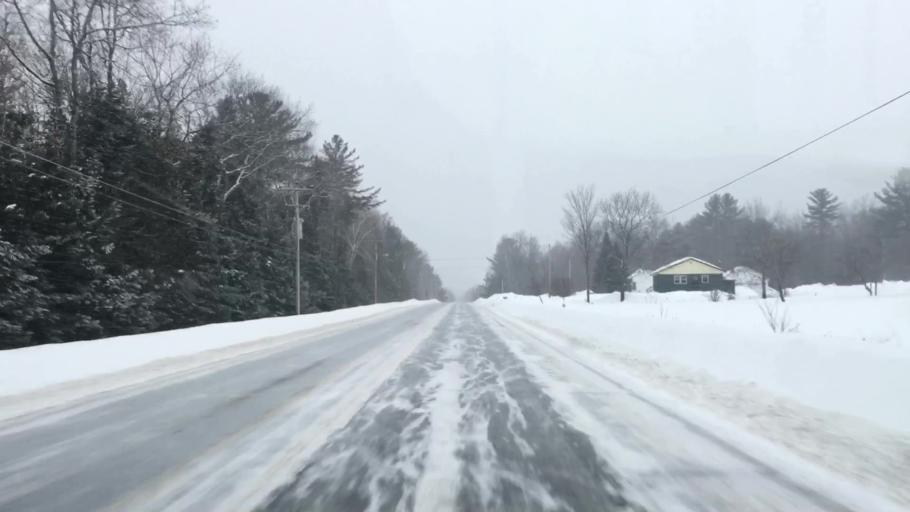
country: US
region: Maine
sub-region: Penobscot County
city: Medway
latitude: 45.5473
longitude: -68.3749
